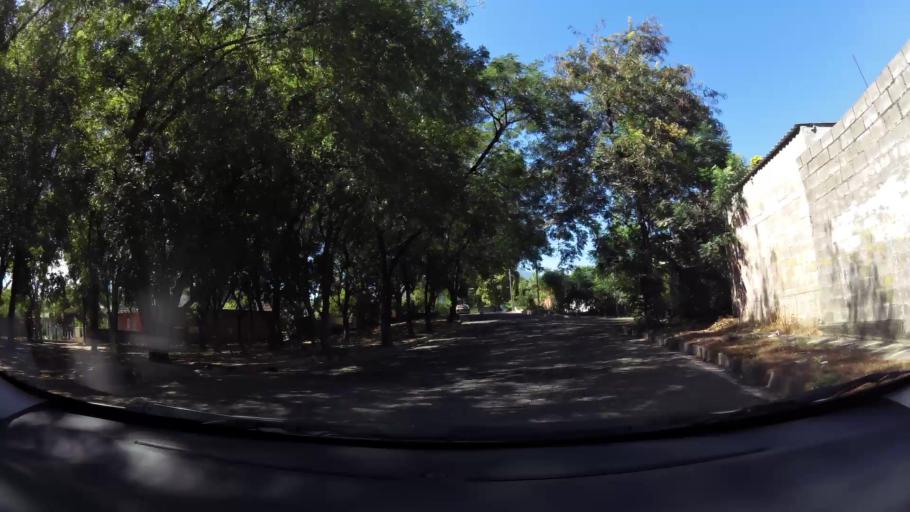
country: SV
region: San Miguel
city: San Miguel
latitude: 13.4793
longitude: -88.1655
